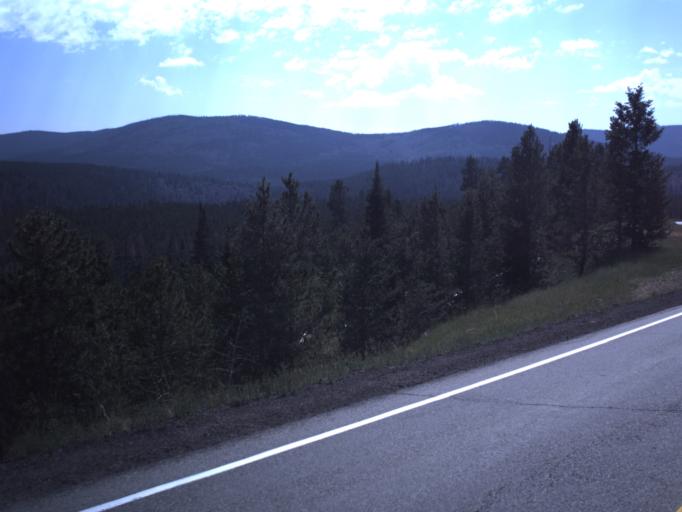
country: US
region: Utah
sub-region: Daggett County
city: Manila
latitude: 40.8366
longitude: -109.4646
